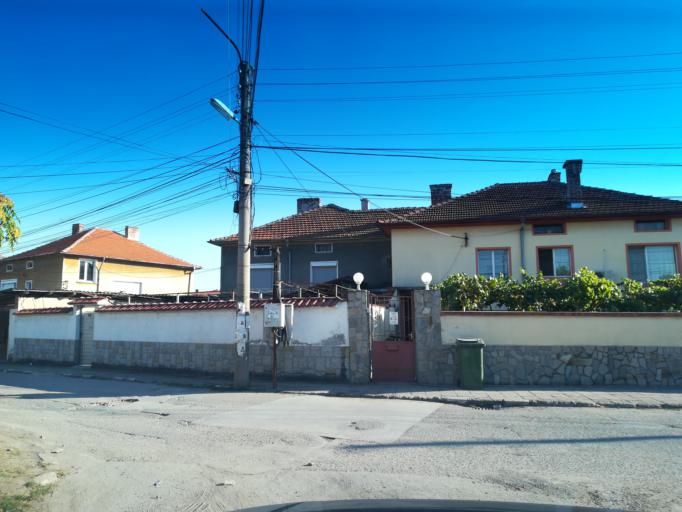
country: BG
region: Stara Zagora
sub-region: Obshtina Chirpan
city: Chirpan
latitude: 42.1049
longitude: 25.2194
